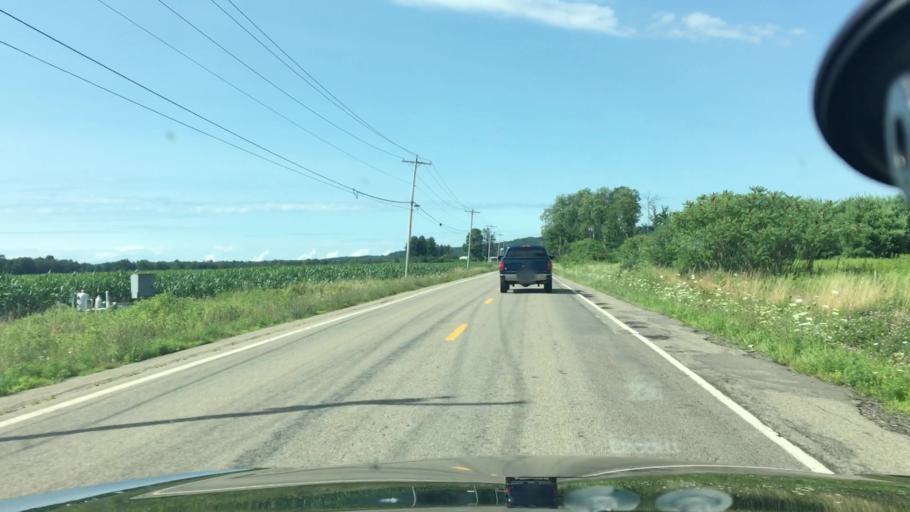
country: US
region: New York
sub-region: Chautauqua County
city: Brocton
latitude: 42.2936
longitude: -79.3530
